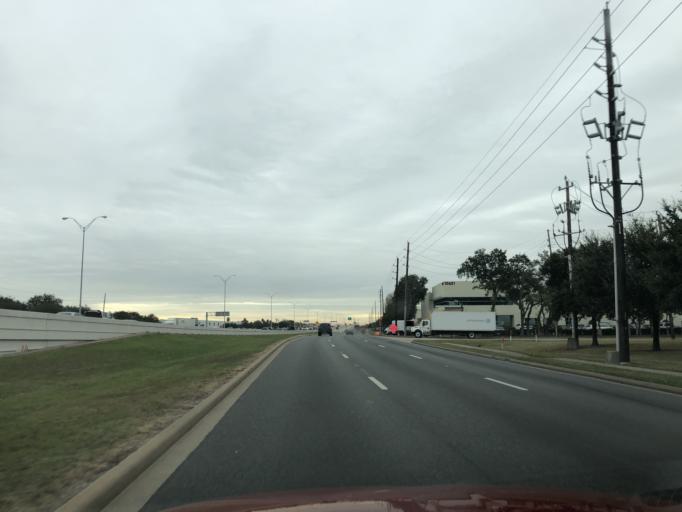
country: US
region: Texas
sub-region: Fort Bend County
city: Missouri City
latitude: 29.6426
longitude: -95.5379
